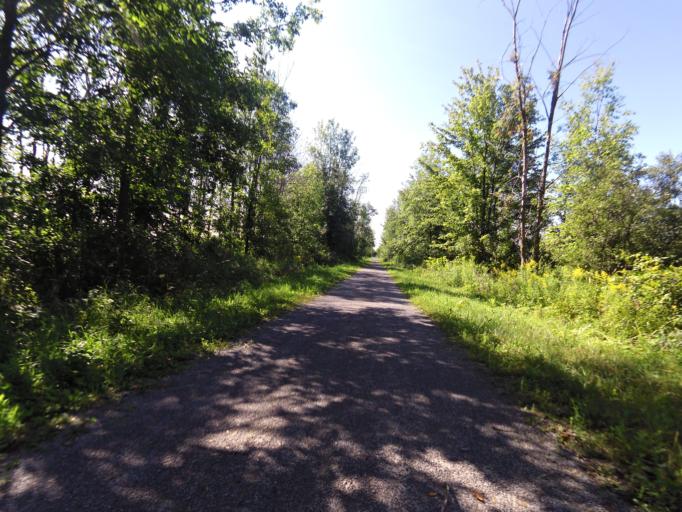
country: CA
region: Ontario
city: Ottawa
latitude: 45.1682
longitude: -75.6166
